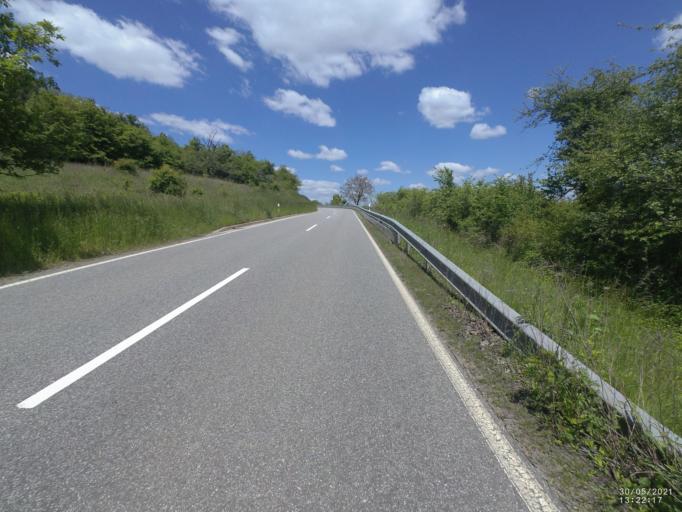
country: DE
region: Rheinland-Pfalz
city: Rhens
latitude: 50.2837
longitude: 7.6104
